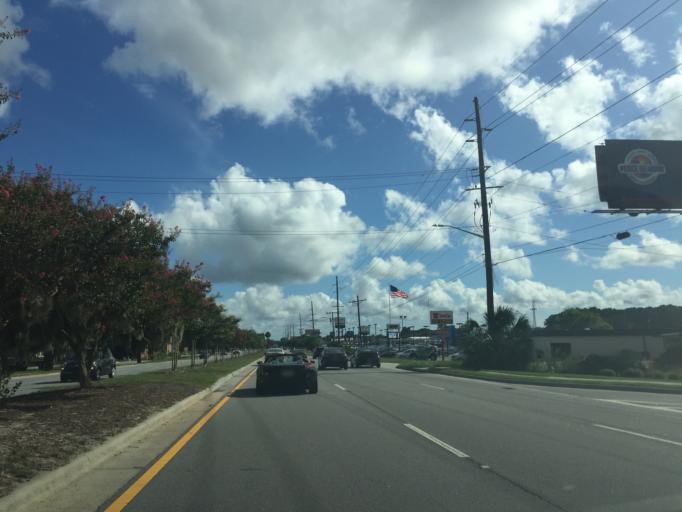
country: US
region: Georgia
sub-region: Chatham County
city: Montgomery
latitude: 31.9968
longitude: -81.1282
